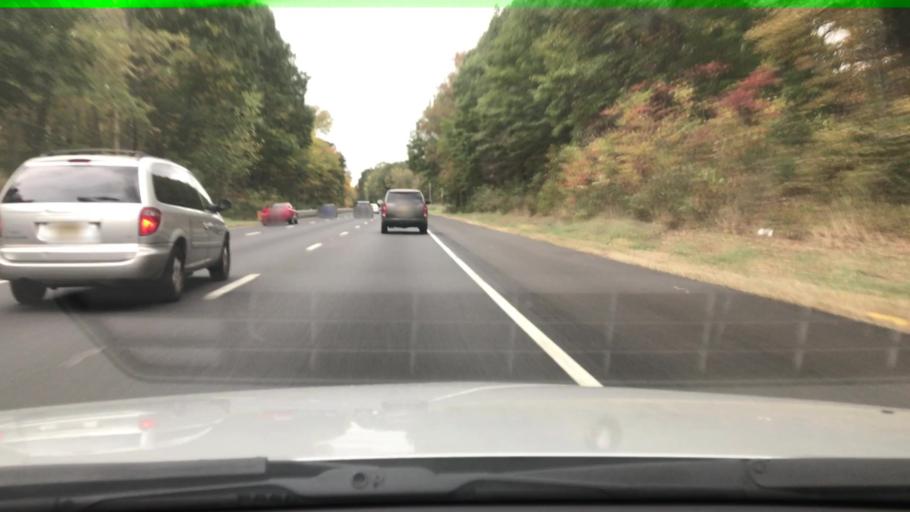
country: US
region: New Jersey
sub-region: Burlington County
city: Roebling
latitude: 40.0637
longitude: -74.8020
